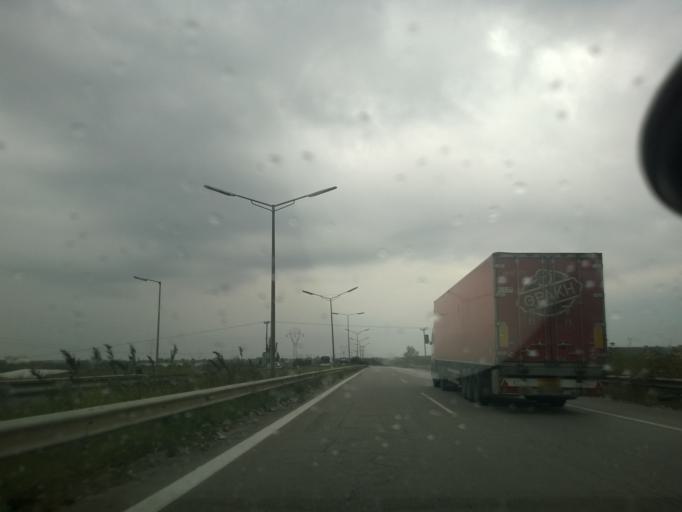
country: GR
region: Central Macedonia
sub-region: Nomos Thessalonikis
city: Agios Athanasios
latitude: 40.7233
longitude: 22.7116
